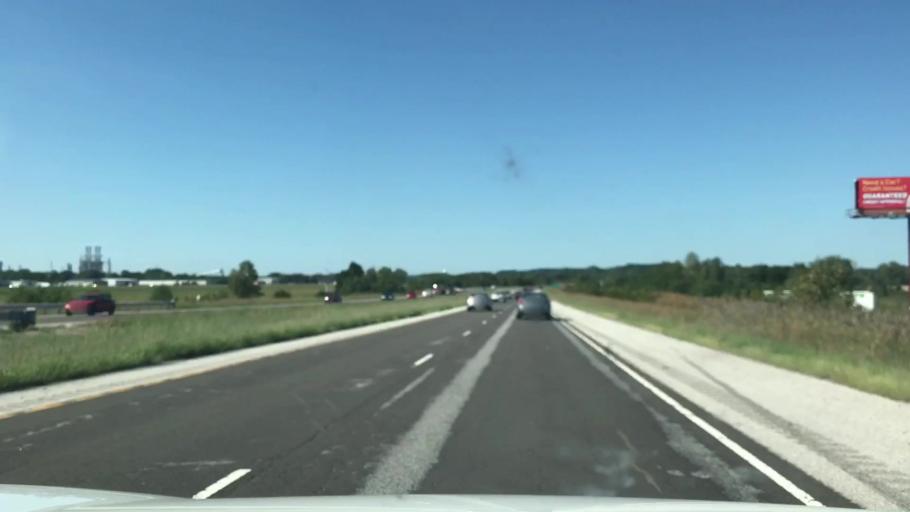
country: US
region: Illinois
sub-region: Madison County
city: South Roxana
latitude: 38.8211
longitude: -90.0425
